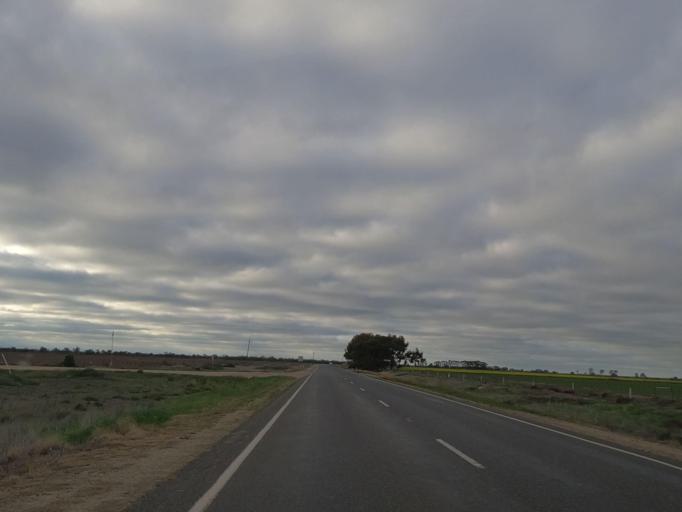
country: AU
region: Victoria
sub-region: Swan Hill
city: Swan Hill
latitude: -35.8318
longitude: 143.9438
